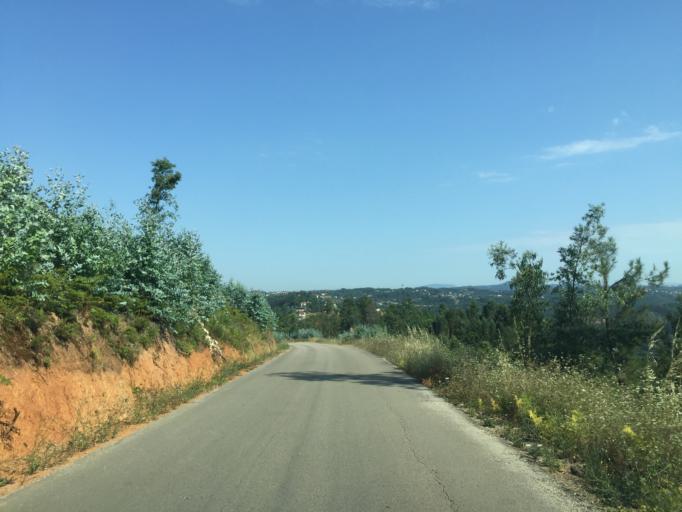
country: PT
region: Santarem
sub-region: Ferreira do Zezere
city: Ferreira do Zezere
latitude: 39.6000
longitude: -8.2923
